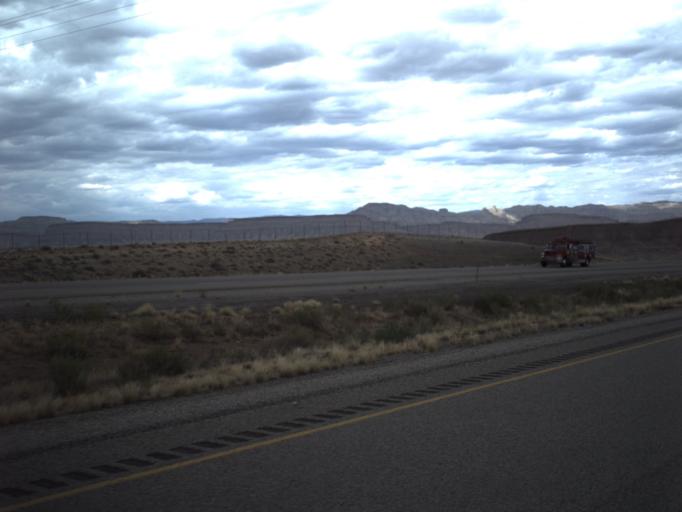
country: US
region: Utah
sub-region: Carbon County
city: East Carbon City
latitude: 38.9752
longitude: -110.1328
